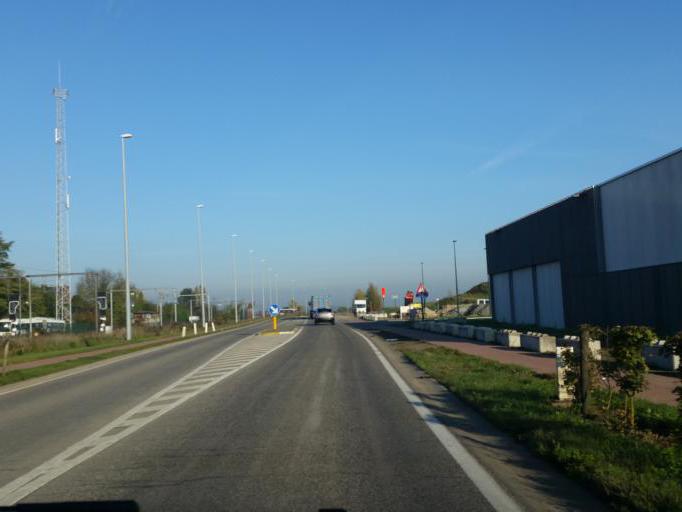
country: BE
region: Flanders
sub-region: Provincie Vlaams-Brabant
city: Asse
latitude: 50.9075
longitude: 4.2084
